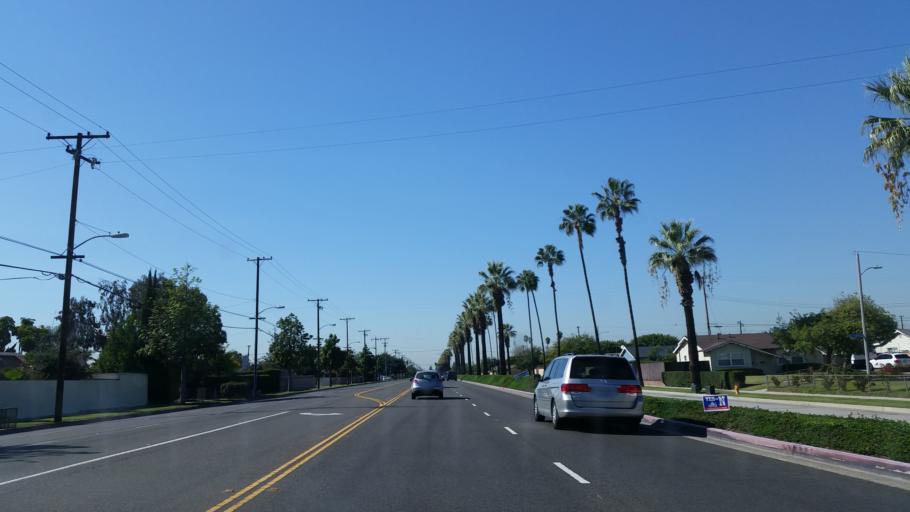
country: US
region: California
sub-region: Orange County
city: Buena Park
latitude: 33.8466
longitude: -118.0158
